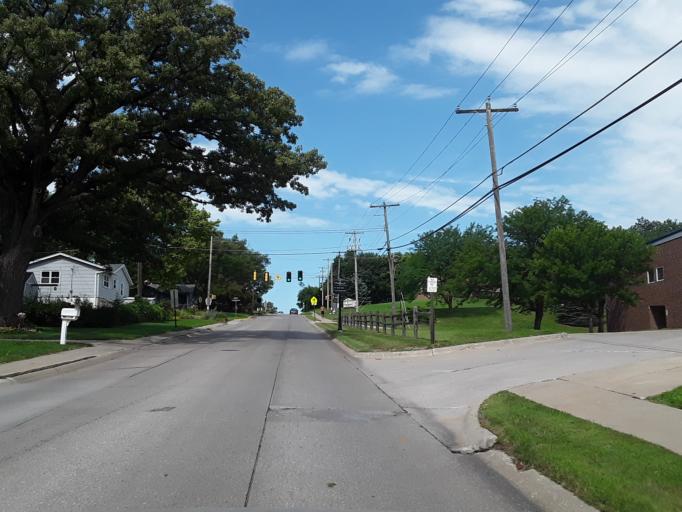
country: US
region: Nebraska
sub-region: Cass County
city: Plattsmouth
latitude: 41.0025
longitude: -95.8997
